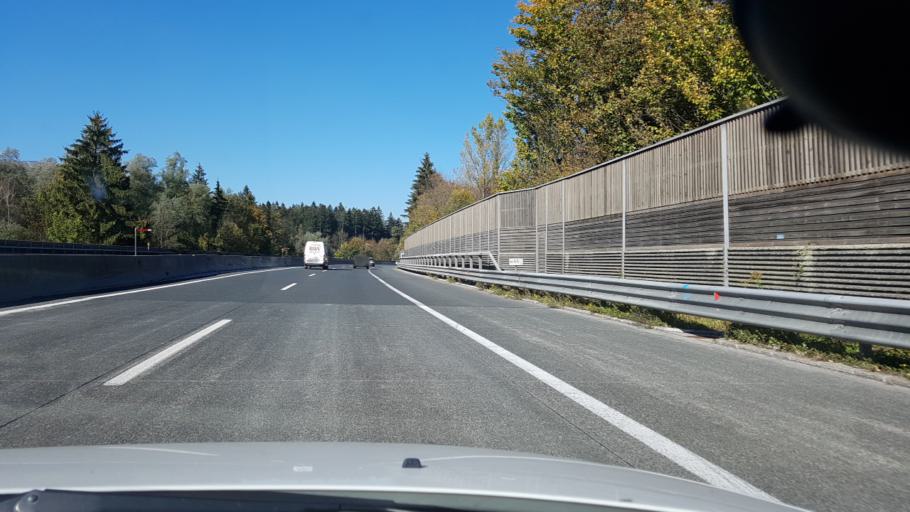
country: AT
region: Salzburg
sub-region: Politischer Bezirk Hallein
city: Adnet
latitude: 47.6578
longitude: 13.1330
